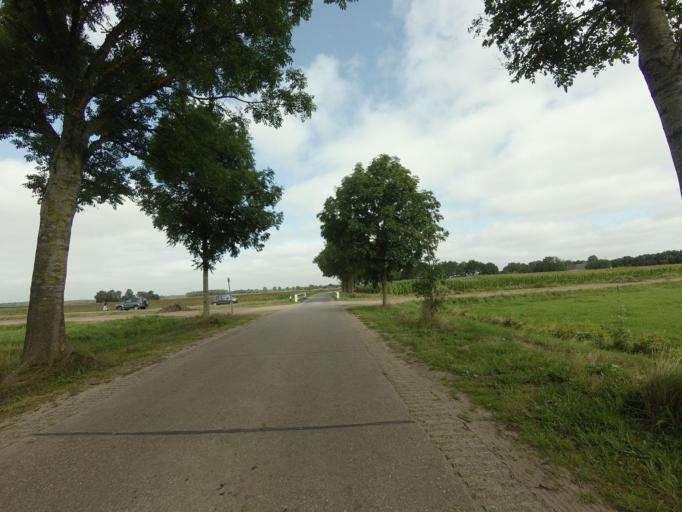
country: NL
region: Drenthe
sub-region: Gemeente Westerveld
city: Havelte
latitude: 52.8382
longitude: 6.2347
